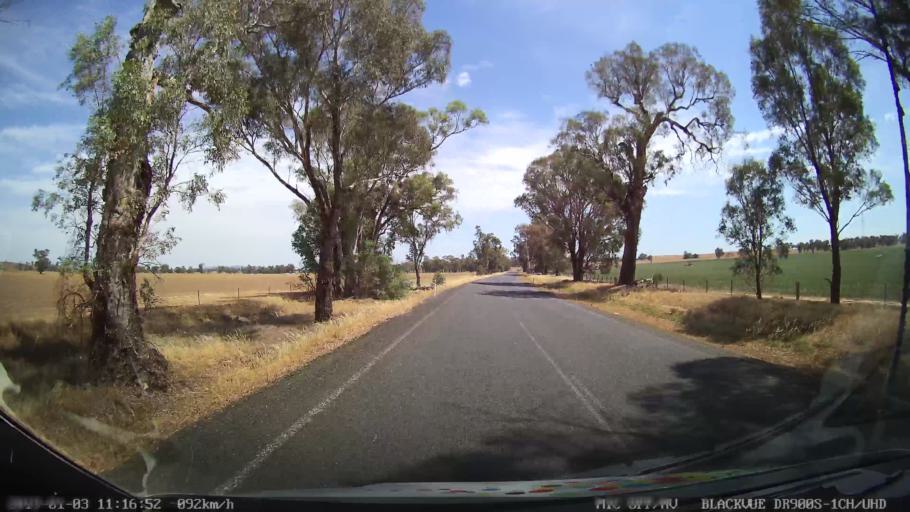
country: AU
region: New South Wales
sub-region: Young
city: Young
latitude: -34.1463
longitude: 148.2681
